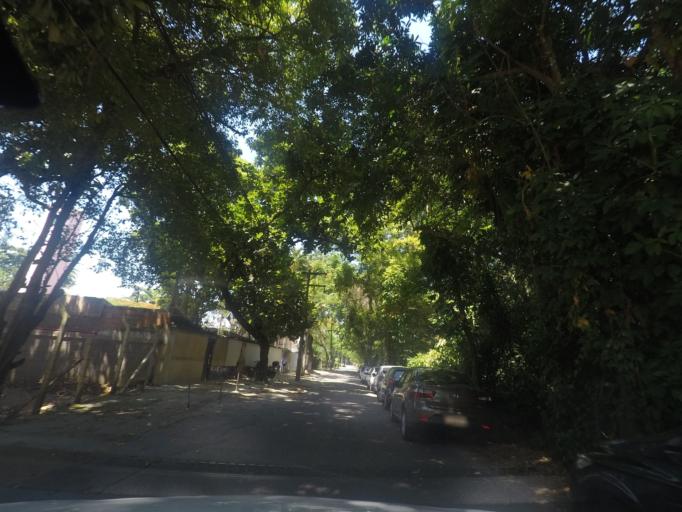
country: BR
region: Rio de Janeiro
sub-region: Nilopolis
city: Nilopolis
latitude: -22.9788
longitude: -43.4566
